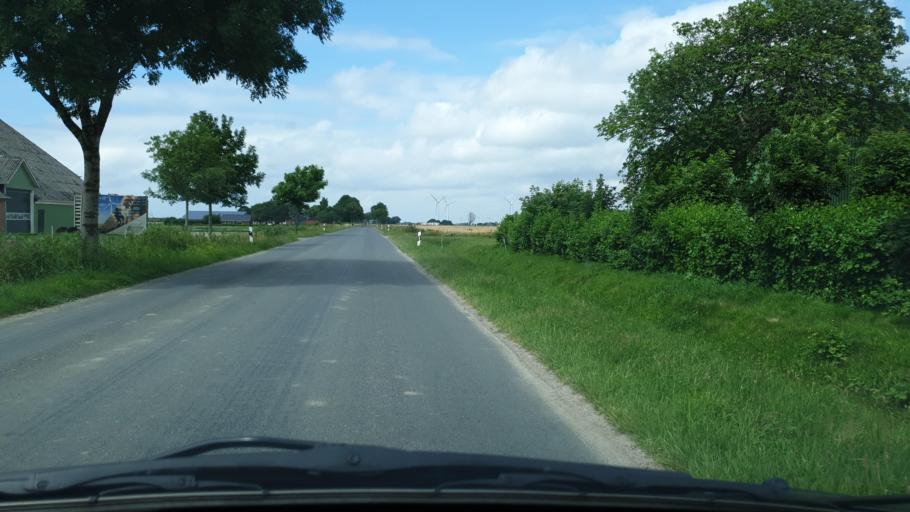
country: DE
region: Schleswig-Holstein
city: Kronprinzenkoog
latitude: 53.9641
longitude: 8.9309
